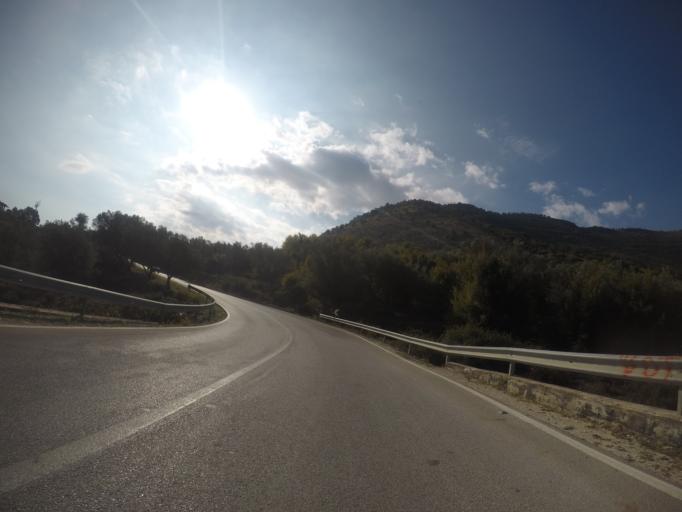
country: AL
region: Vlore
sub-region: Rrethi i Sarandes
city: Sarande
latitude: 39.9275
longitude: 19.9796
